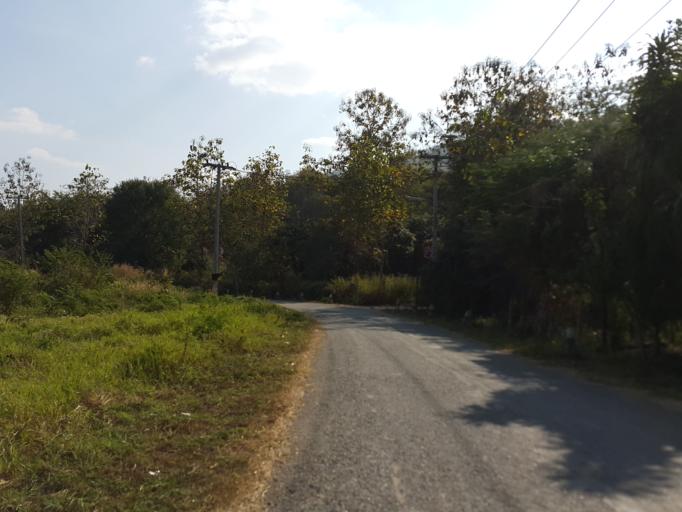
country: TH
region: Chiang Mai
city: Mae On
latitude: 18.8064
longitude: 99.2277
